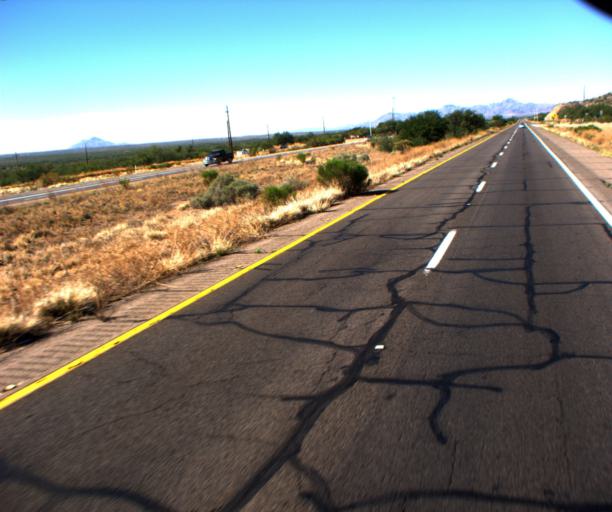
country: US
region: Arizona
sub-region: Pima County
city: Arivaca Junction
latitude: 31.7701
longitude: -111.0338
